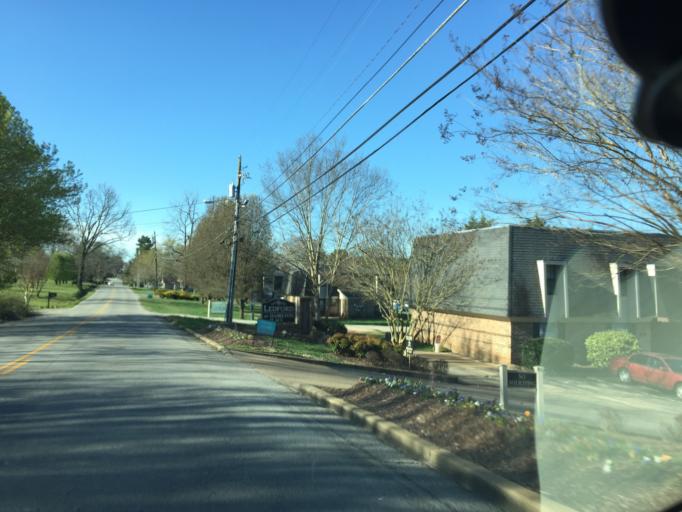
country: US
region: Tennessee
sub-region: Hamilton County
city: East Brainerd
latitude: 35.0257
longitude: -85.1707
